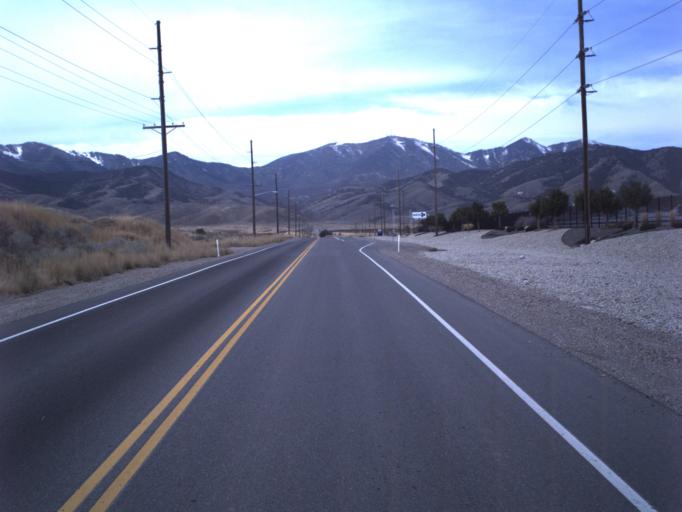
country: US
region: Utah
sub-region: Salt Lake County
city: Oquirrh
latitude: 40.6532
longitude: -112.0615
